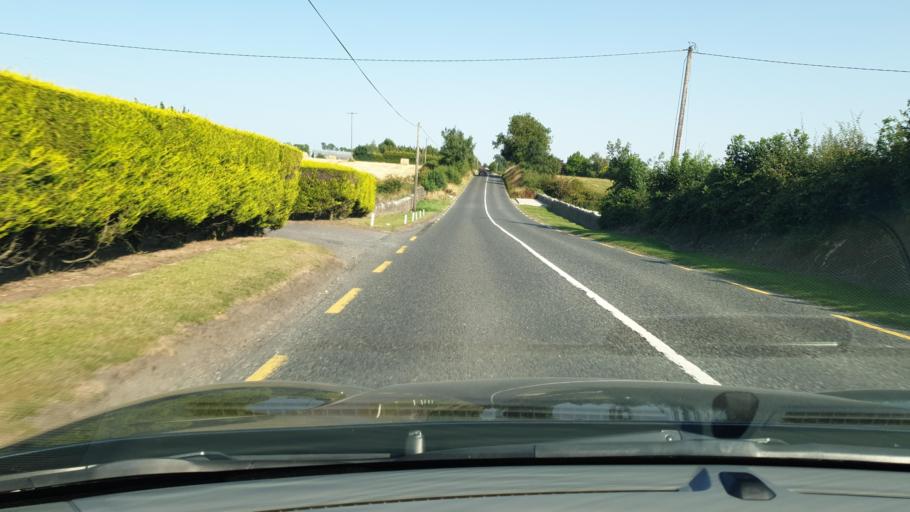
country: IE
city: Kentstown
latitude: 53.6365
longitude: -6.5987
